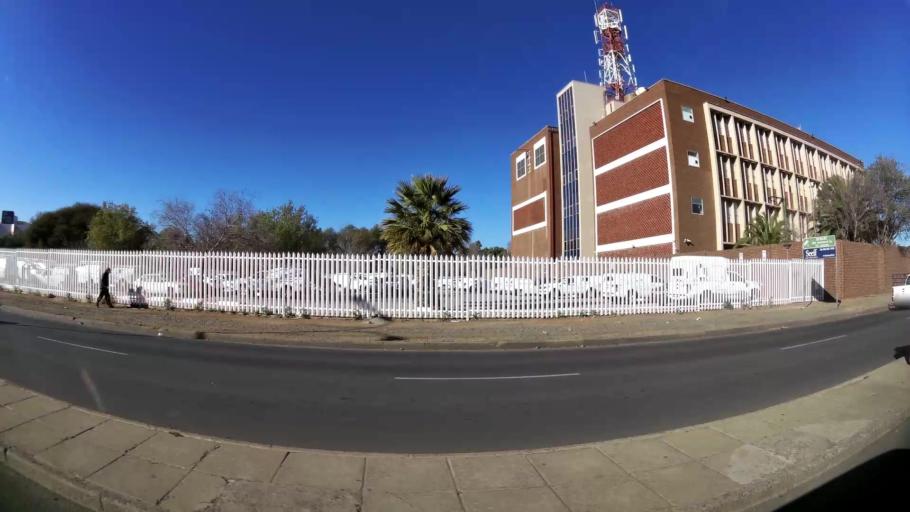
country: ZA
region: Northern Cape
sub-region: Frances Baard District Municipality
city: Kimberley
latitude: -28.7424
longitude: 24.7674
